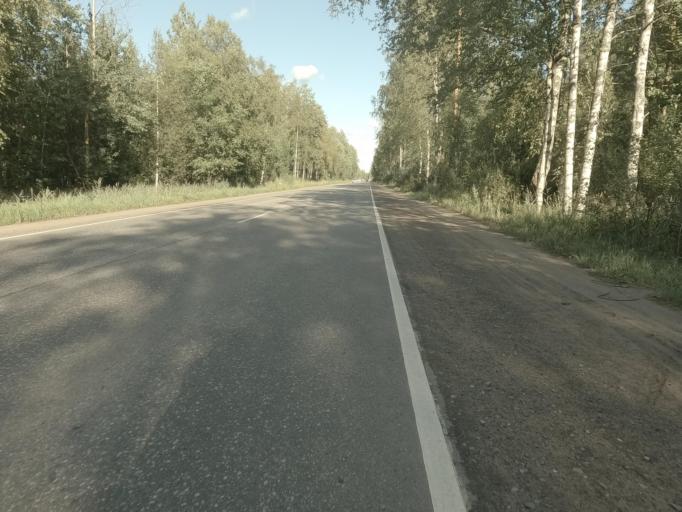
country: RU
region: Leningrad
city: Imeni Morozova
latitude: 59.9740
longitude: 30.9961
